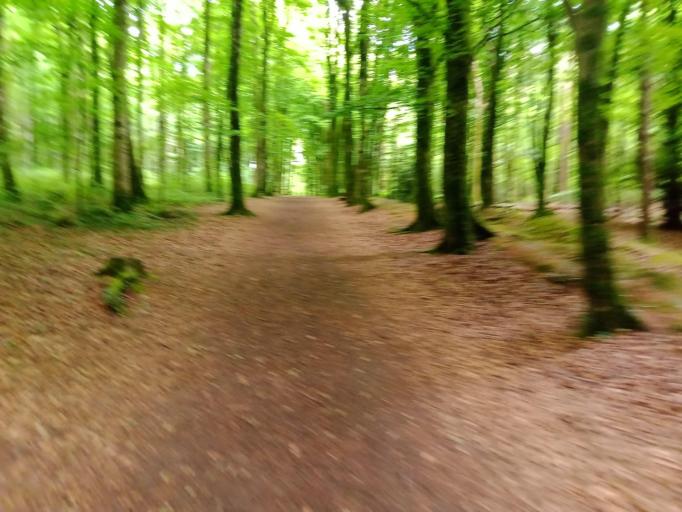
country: IE
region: Leinster
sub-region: Laois
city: Stradbally
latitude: 53.0036
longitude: -7.1231
